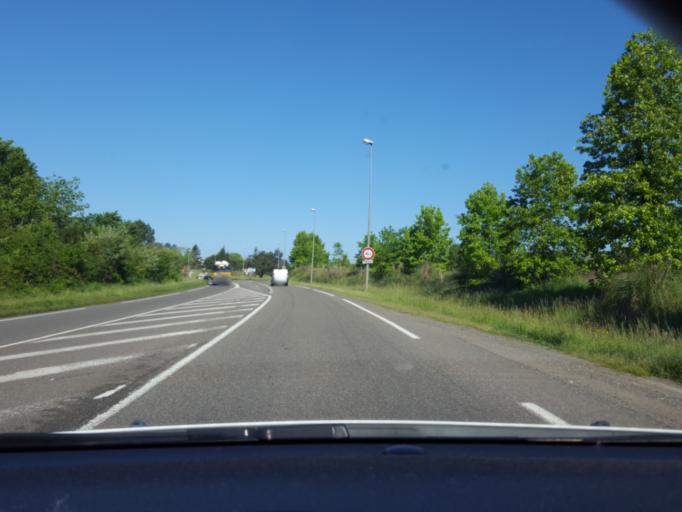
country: FR
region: Aquitaine
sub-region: Departement des Landes
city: Tarnos
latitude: 43.5510
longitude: -1.4541
